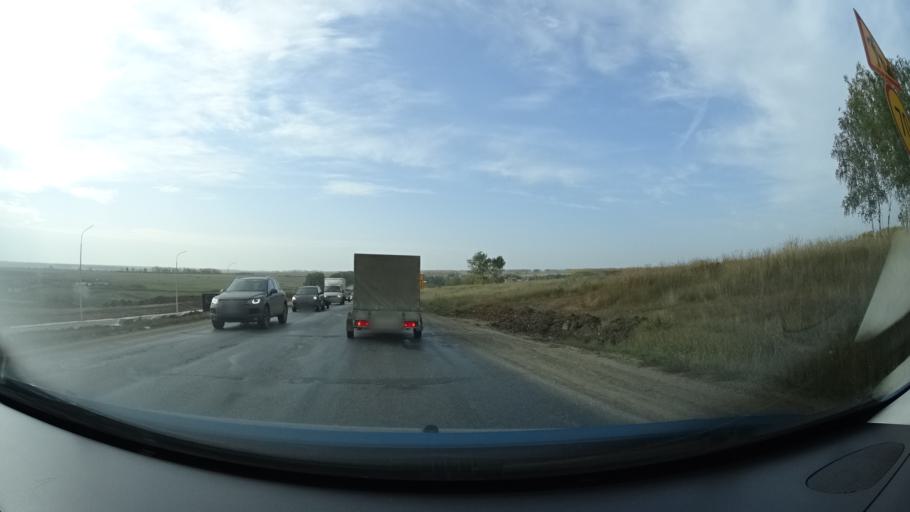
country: RU
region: Bashkortostan
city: Buzdyak
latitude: 54.6335
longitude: 54.4707
